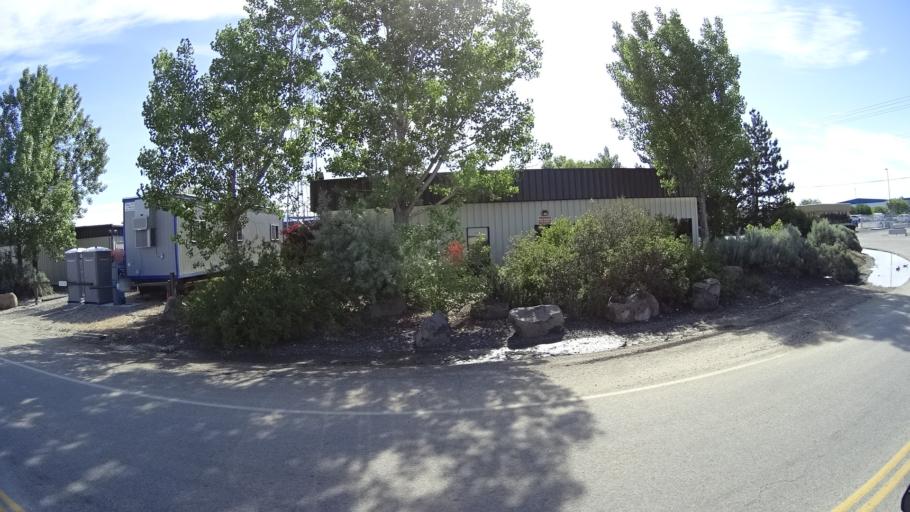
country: US
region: Idaho
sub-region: Ada County
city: Boise
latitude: 43.5647
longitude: -116.2074
